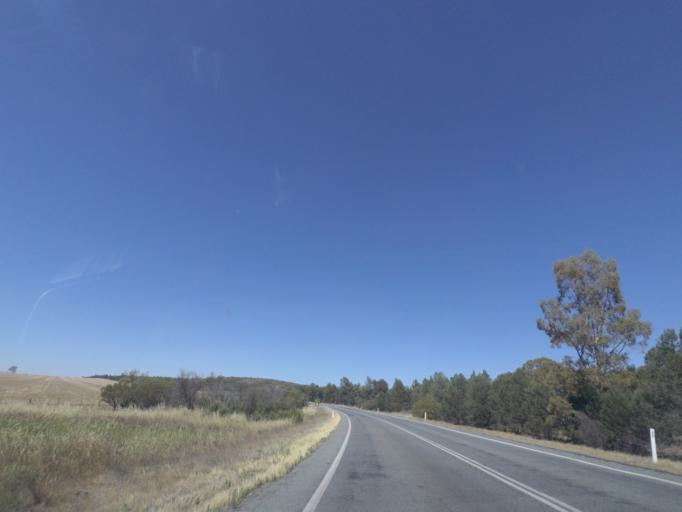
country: AU
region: New South Wales
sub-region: Narrandera
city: Narrandera
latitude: -34.4196
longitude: 146.8472
